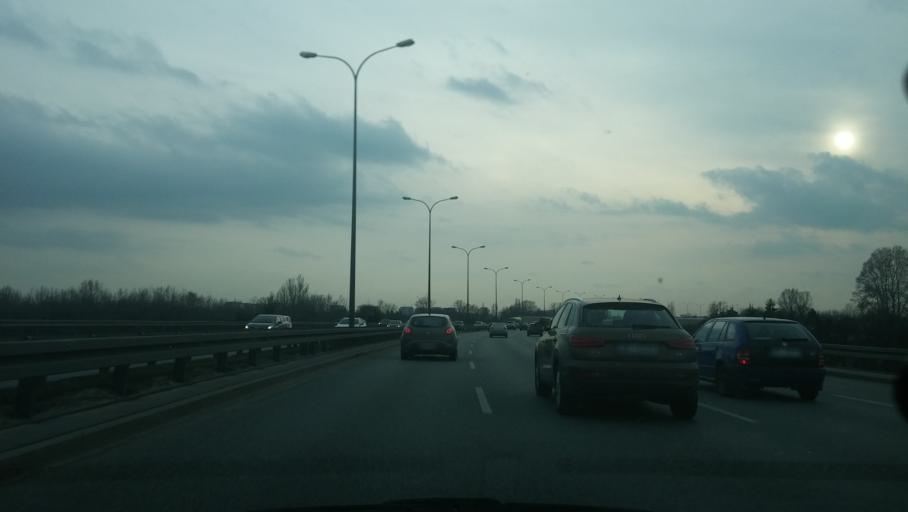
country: PL
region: Masovian Voivodeship
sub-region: Warszawa
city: Praga Poludnie
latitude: 52.2061
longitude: 21.0823
